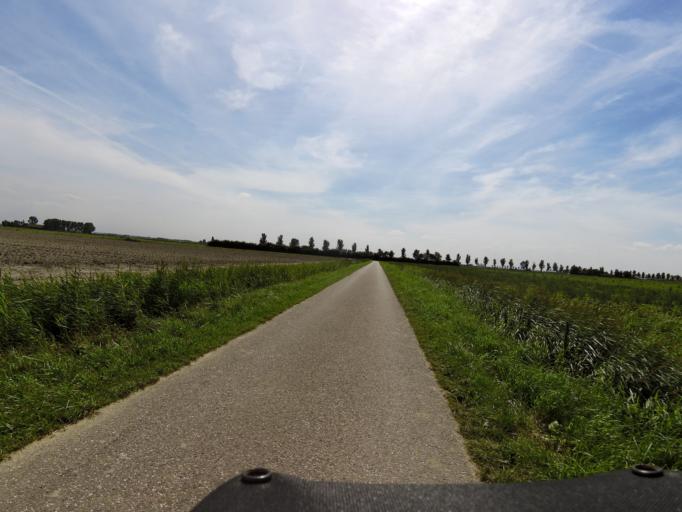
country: NL
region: South Holland
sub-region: Gemeente Goeree-Overflakkee
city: Middelharnis
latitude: 51.7504
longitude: 4.1333
